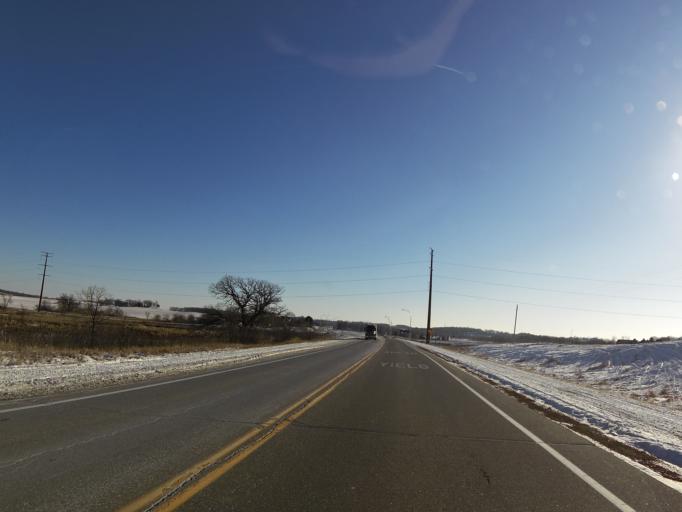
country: US
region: Minnesota
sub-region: Le Sueur County
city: New Prague
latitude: 44.5754
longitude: -93.5063
